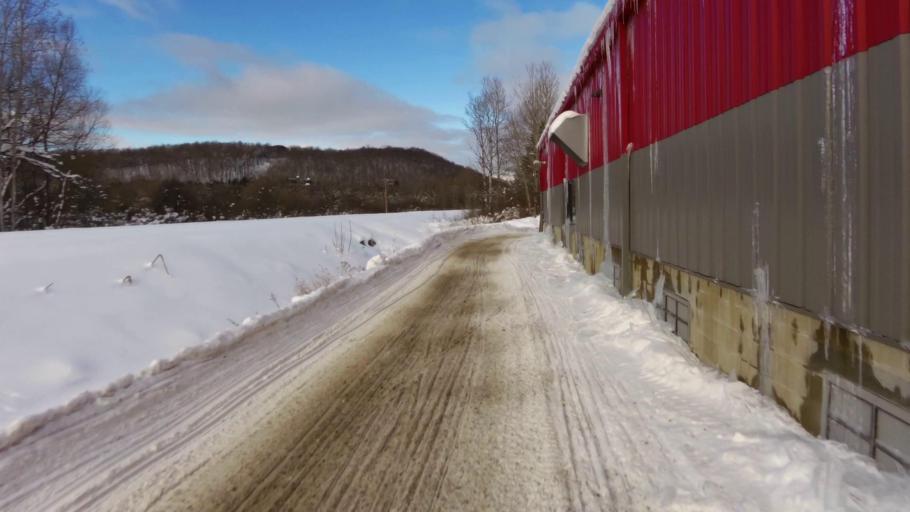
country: US
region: New York
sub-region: Cattaraugus County
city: Franklinville
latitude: 42.3395
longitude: -78.4613
